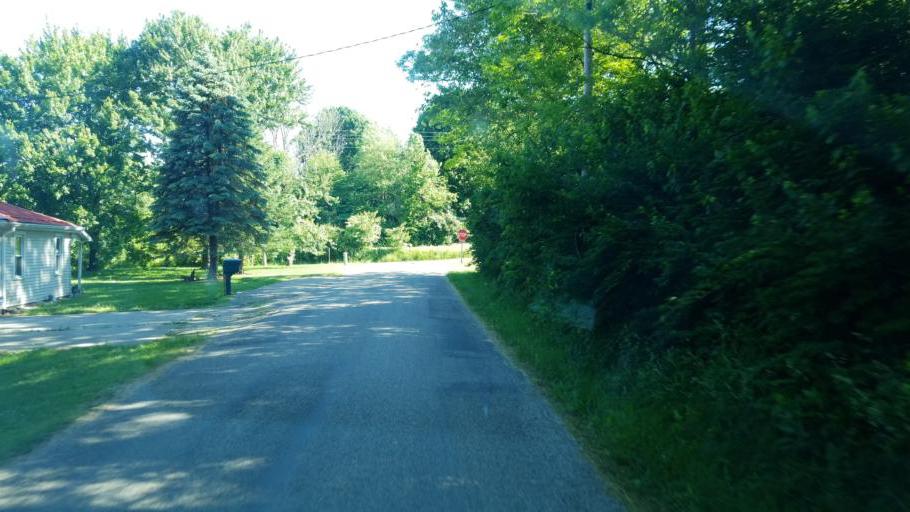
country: US
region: Ohio
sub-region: Preble County
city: New Paris
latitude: 39.8726
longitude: -84.8323
